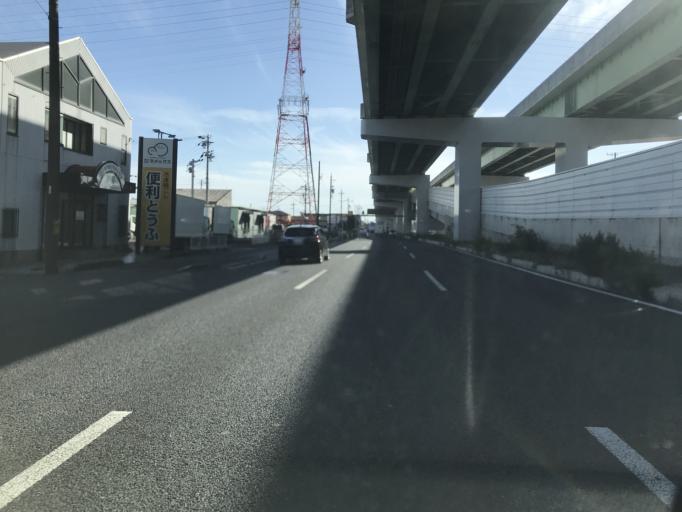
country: JP
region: Aichi
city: Iwakura
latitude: 35.2536
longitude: 136.8435
